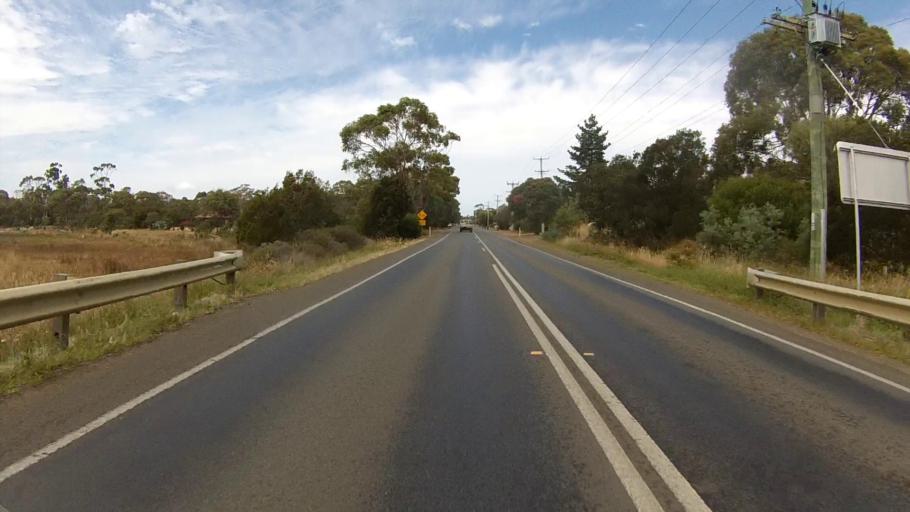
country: AU
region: Tasmania
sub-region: Clarence
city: Sandford
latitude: -42.9362
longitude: 147.4932
